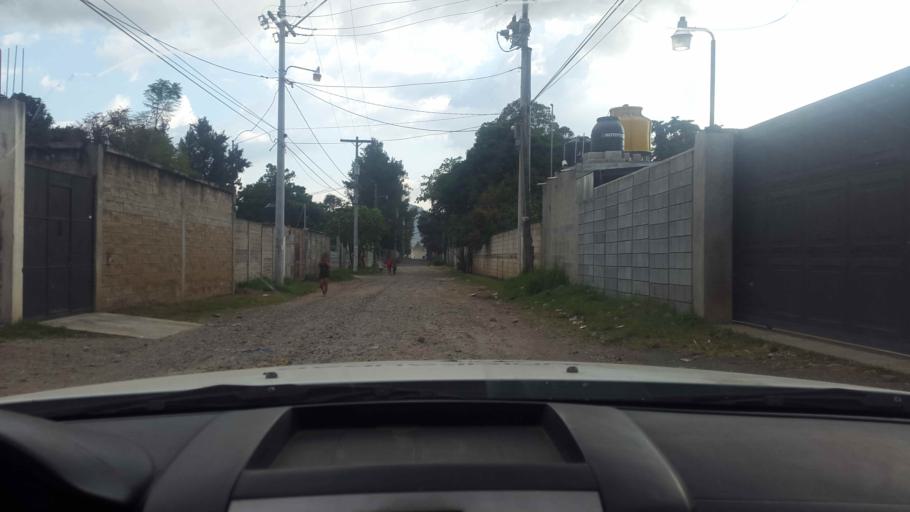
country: GT
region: Guatemala
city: Petapa
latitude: 14.5140
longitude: -90.5394
